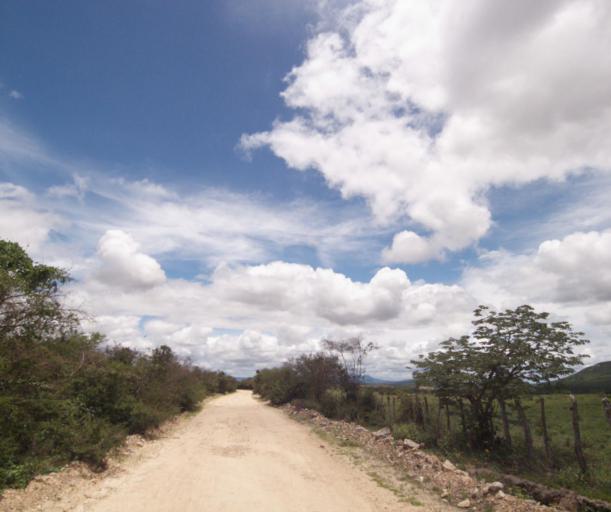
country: BR
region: Bahia
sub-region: Tanhacu
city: Tanhacu
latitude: -14.1711
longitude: -41.1379
